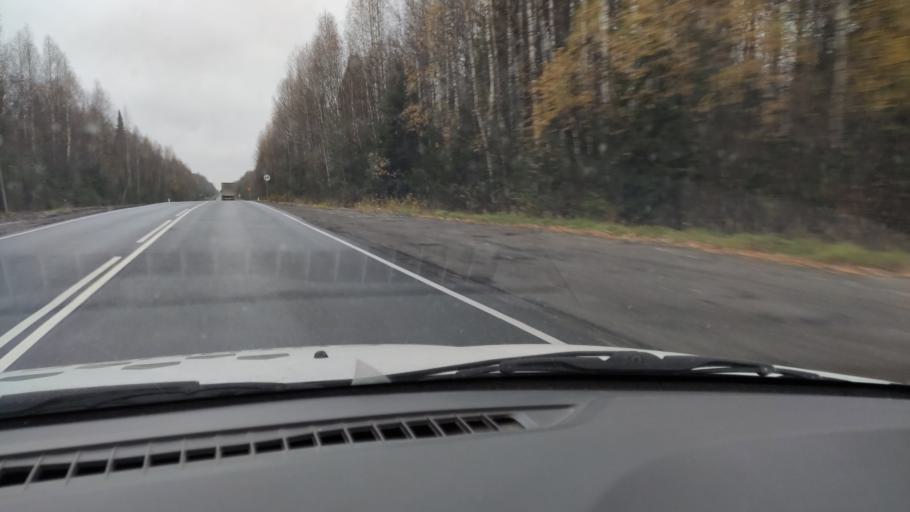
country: RU
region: Kirov
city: Omutninsk
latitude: 58.7640
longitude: 51.9924
